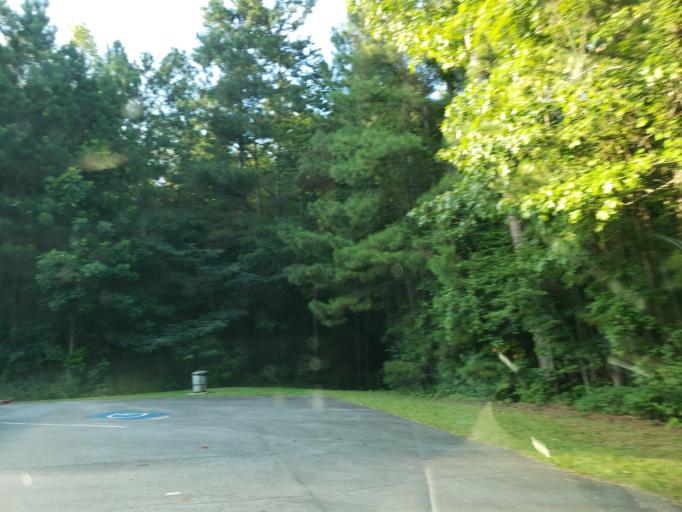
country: US
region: Georgia
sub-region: Bartow County
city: Emerson
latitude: 34.1890
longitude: -84.6949
